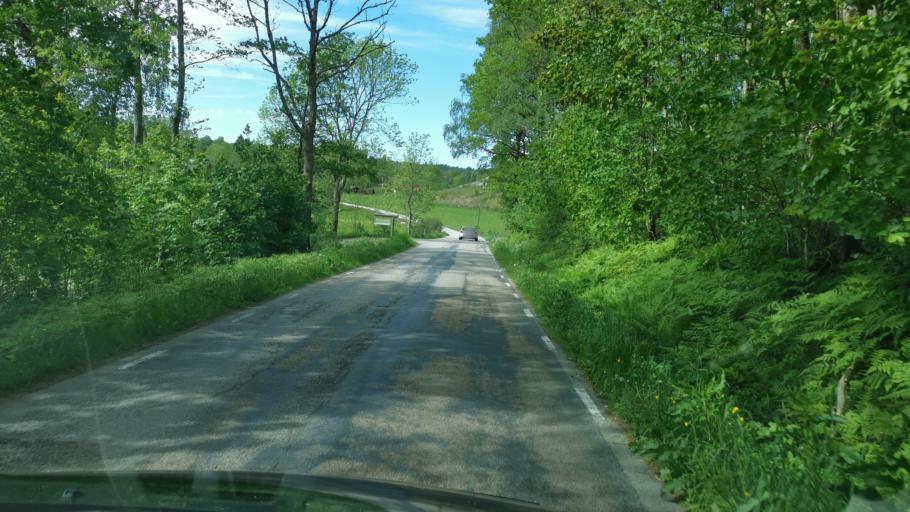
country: SE
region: Vaestra Goetaland
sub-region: Orust
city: Henan
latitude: 58.2683
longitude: 11.6057
